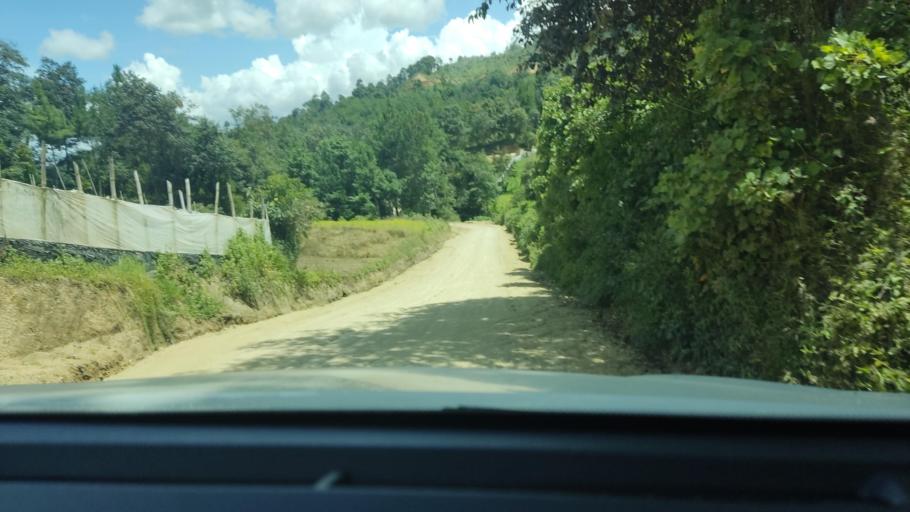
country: GT
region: Chimaltenango
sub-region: Municipio de San Juan Comalapa
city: Comalapa
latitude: 14.7637
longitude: -90.8841
